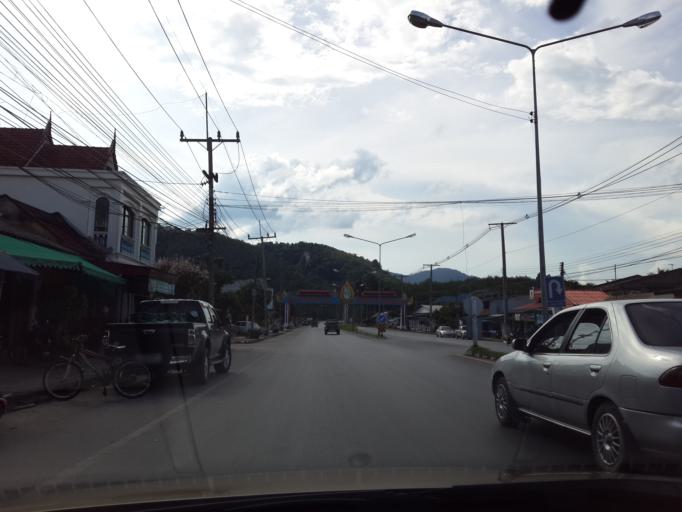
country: TH
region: Yala
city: Krong Pi Nang
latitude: 6.4585
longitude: 101.3356
